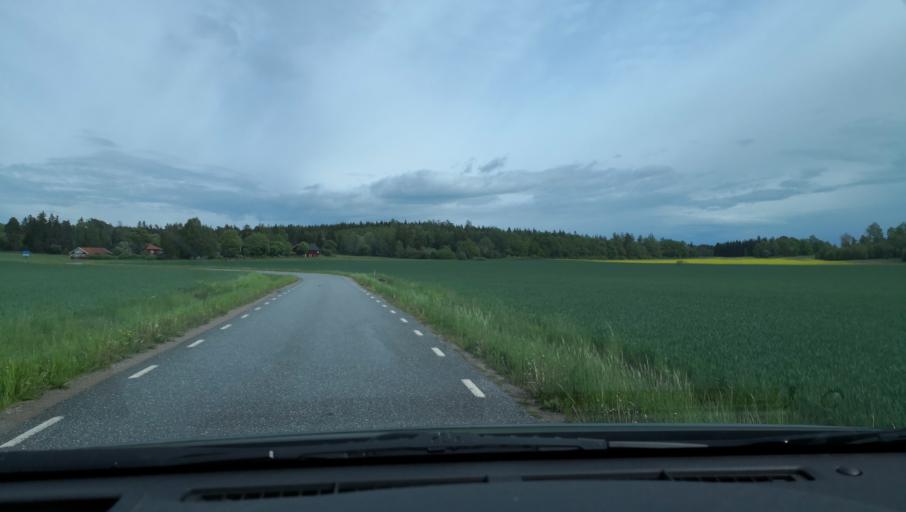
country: SE
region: Uppsala
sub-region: Enkopings Kommun
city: Orsundsbro
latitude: 59.7036
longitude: 17.4152
